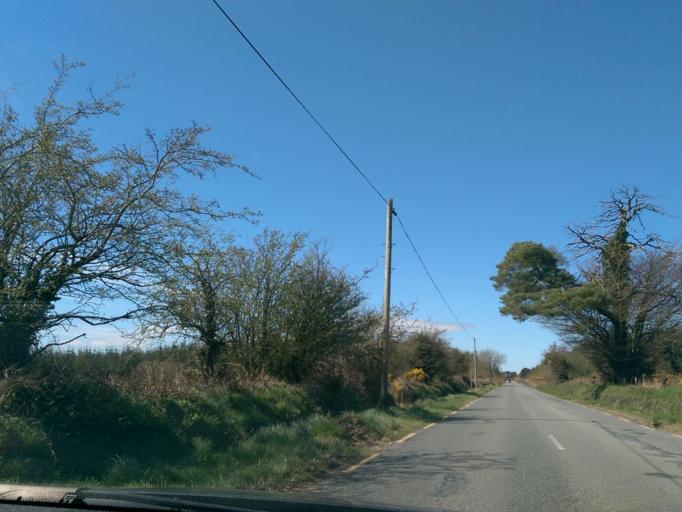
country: IE
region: Leinster
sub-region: Wicklow
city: Carnew
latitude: 52.8227
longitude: -6.5135
